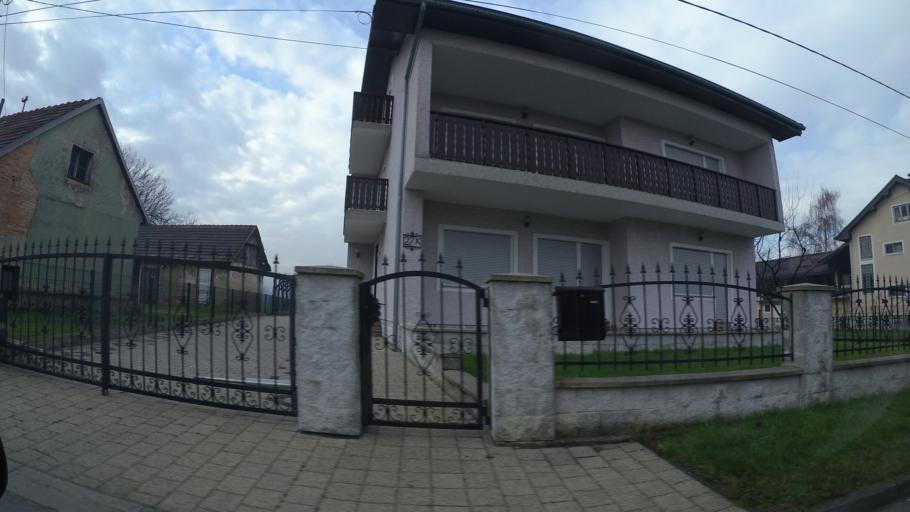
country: HR
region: Karlovacka
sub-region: Grad Karlovac
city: Karlovac
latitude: 45.4977
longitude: 15.5392
